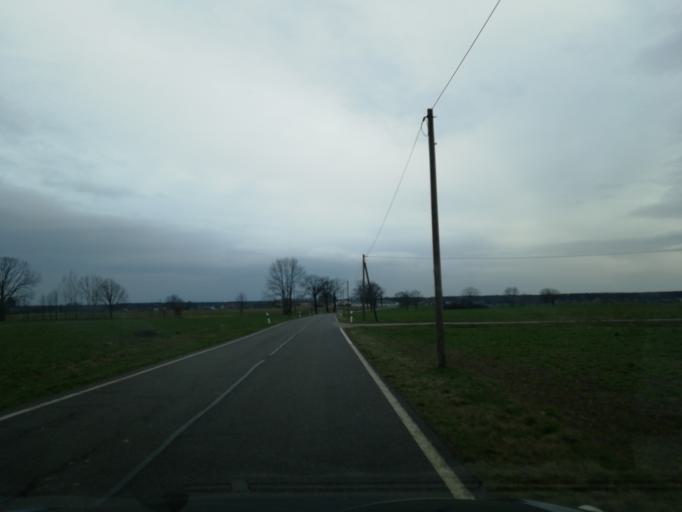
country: DE
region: Brandenburg
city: Calau
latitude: 51.7402
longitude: 14.0239
